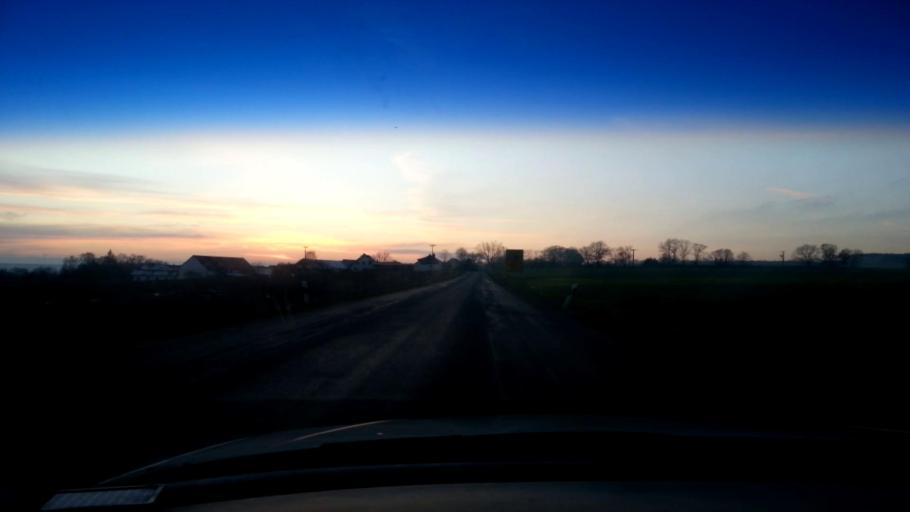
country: DE
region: Bavaria
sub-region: Upper Franconia
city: Pommersfelden
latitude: 49.7800
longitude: 10.8298
